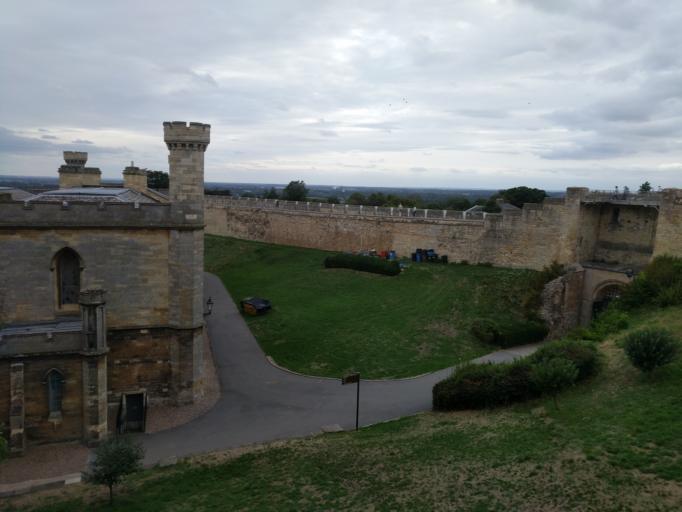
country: GB
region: England
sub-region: Lincolnshire
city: Lincoln
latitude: 53.2357
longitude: -0.5412
